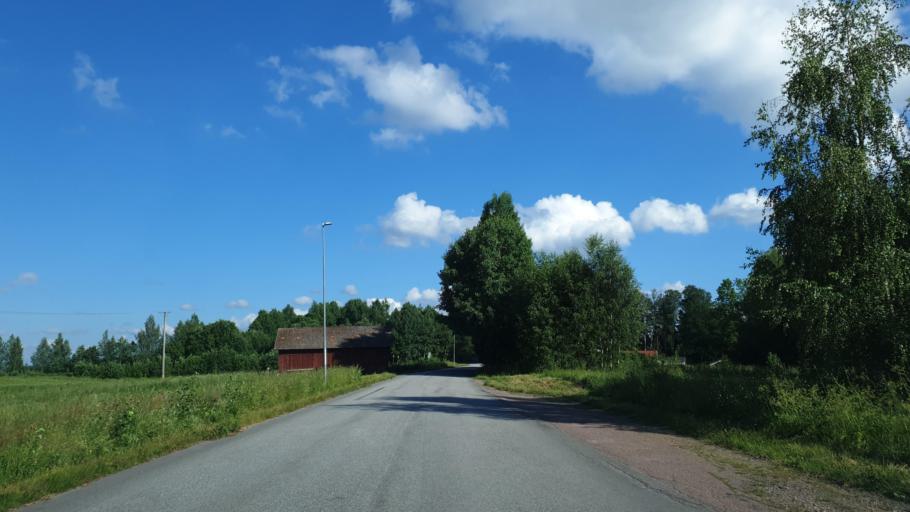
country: SE
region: Dalarna
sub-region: Avesta Kommun
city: Avesta
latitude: 60.1265
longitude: 16.2686
